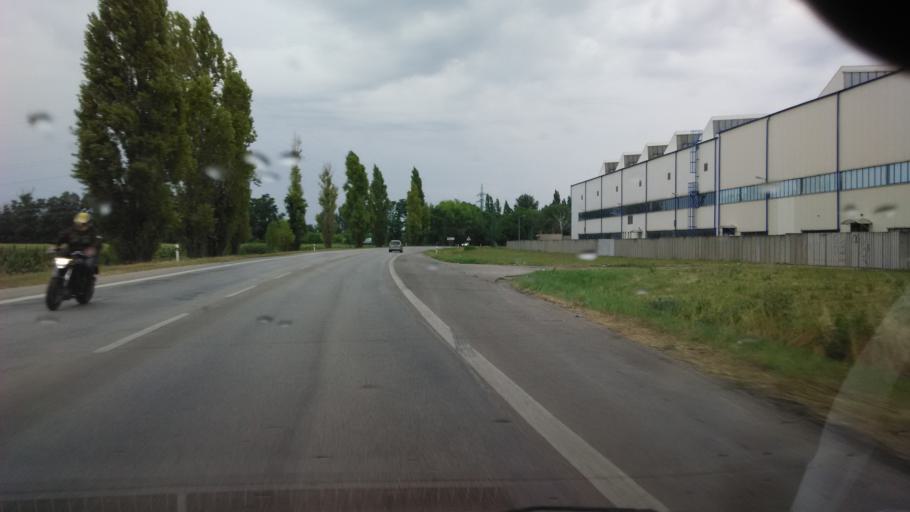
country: SK
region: Trnavsky
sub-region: Okres Trnava
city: Trnava
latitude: 48.3512
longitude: 17.5741
